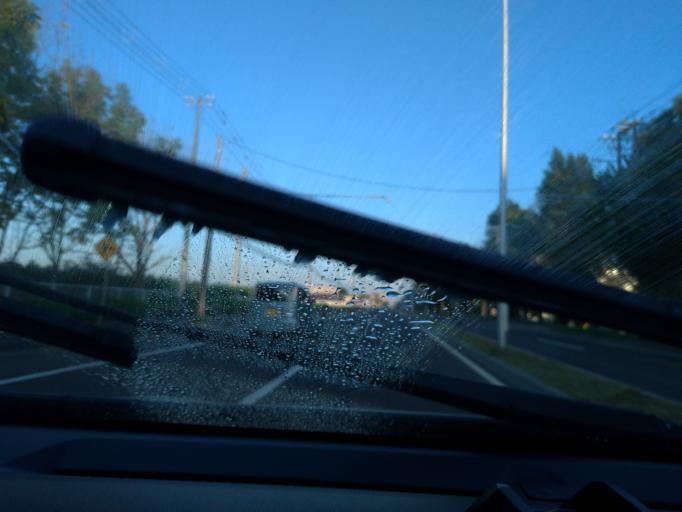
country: JP
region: Hokkaido
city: Ishikari
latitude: 43.1600
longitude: 141.3764
